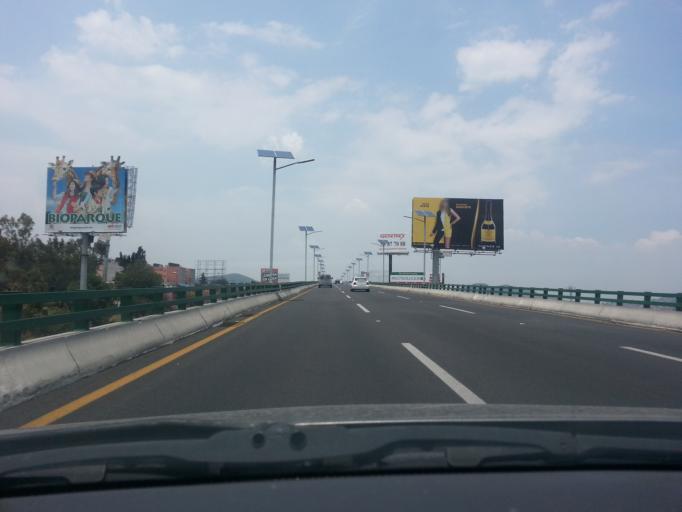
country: MX
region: Mexico
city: Tlalnepantla
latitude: 19.5560
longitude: -99.2061
